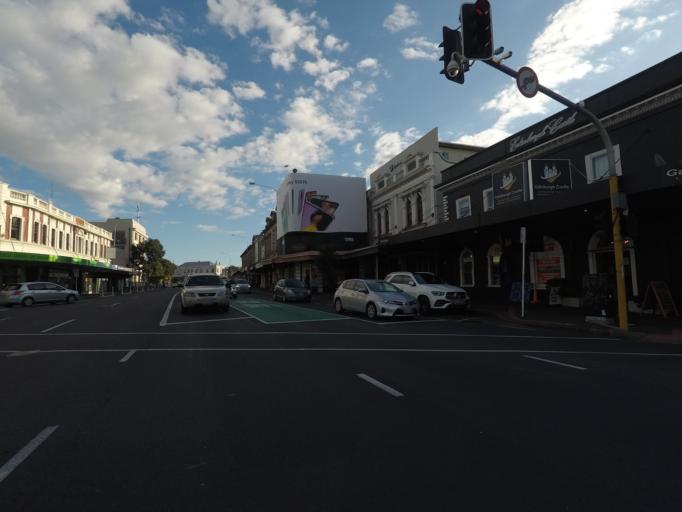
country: NZ
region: Auckland
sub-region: Auckland
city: Auckland
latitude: -36.8639
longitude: 174.7610
